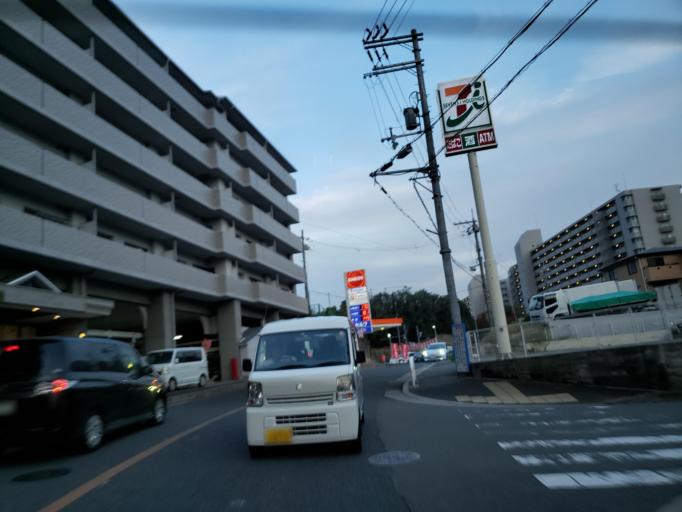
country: JP
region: Osaka
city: Ibaraki
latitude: 34.7988
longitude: 135.5343
